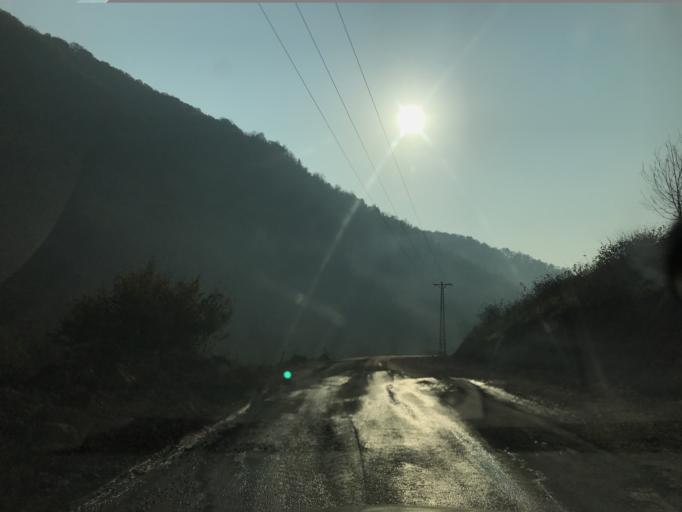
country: TR
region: Duzce
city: Cumayeri
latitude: 40.9280
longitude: 30.9293
